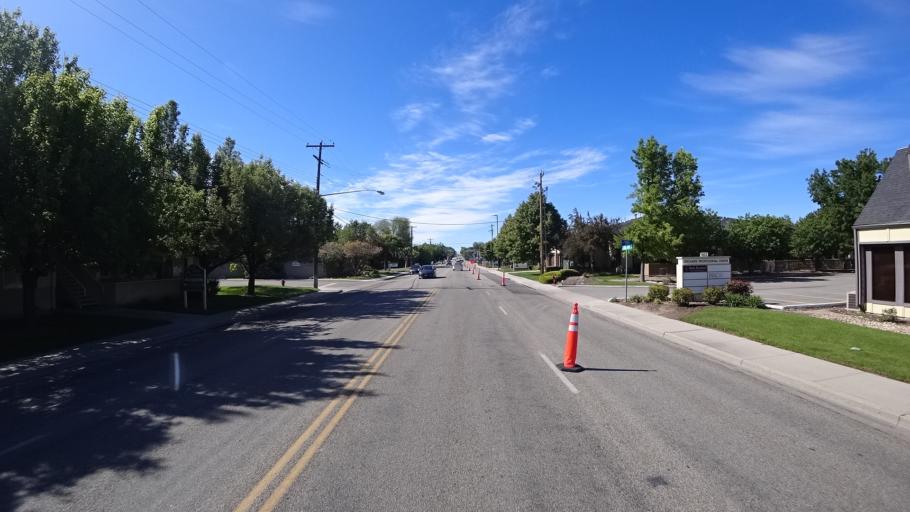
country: US
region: Idaho
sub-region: Ada County
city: Garden City
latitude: 43.5957
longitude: -116.2436
